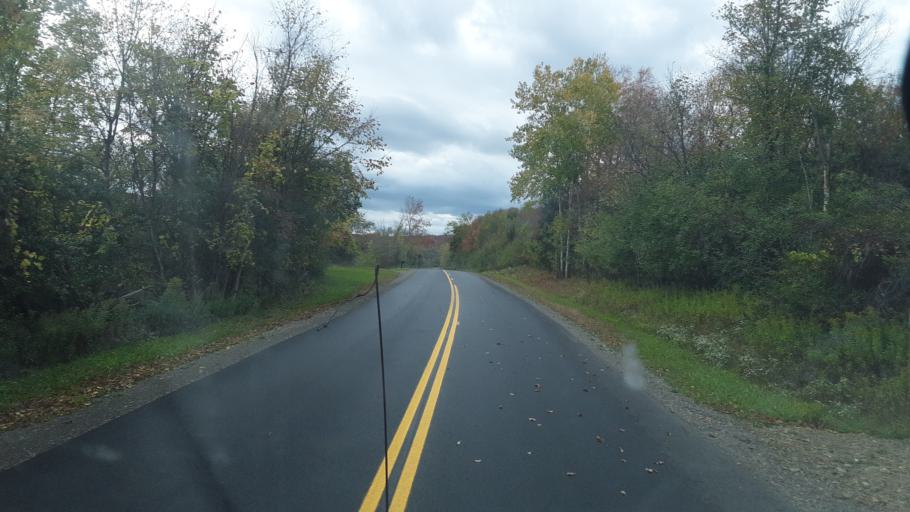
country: US
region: New York
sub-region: Allegany County
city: Alfred
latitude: 42.3684
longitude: -77.8116
